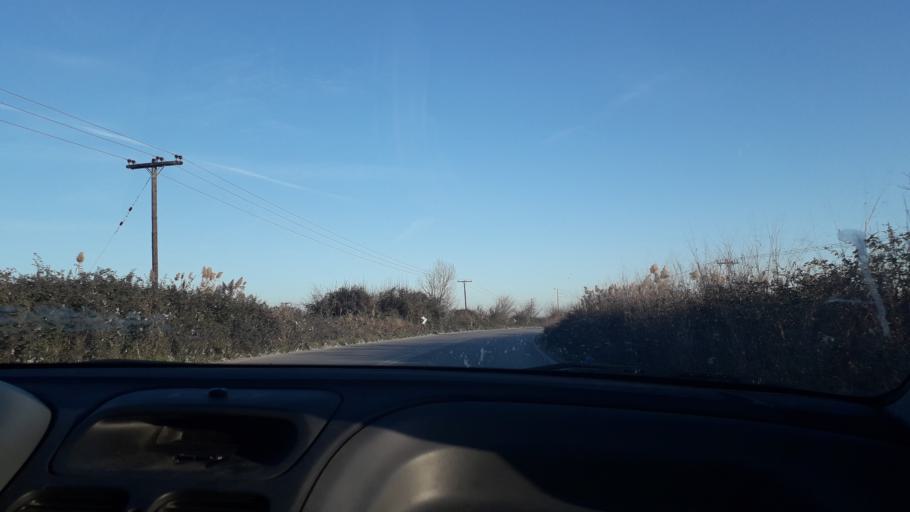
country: GR
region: Central Macedonia
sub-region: Nomos Imathias
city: Agkathia
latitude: 40.5776
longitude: 22.4786
